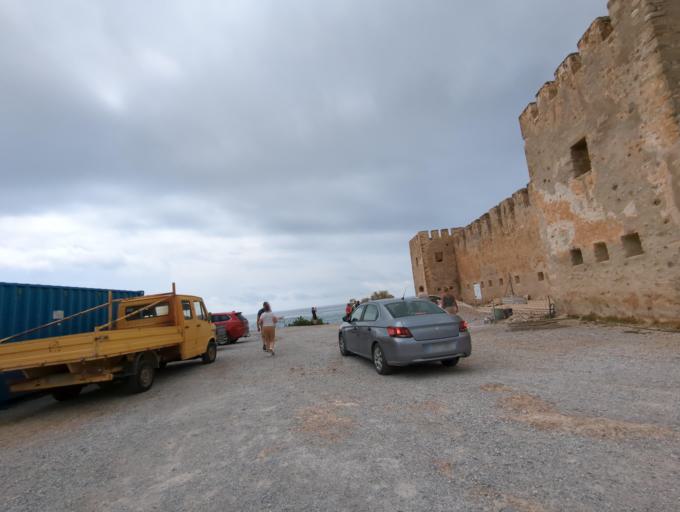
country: GR
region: Crete
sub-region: Nomos Chanias
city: Chora Sfakion
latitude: 35.1822
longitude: 24.2346
